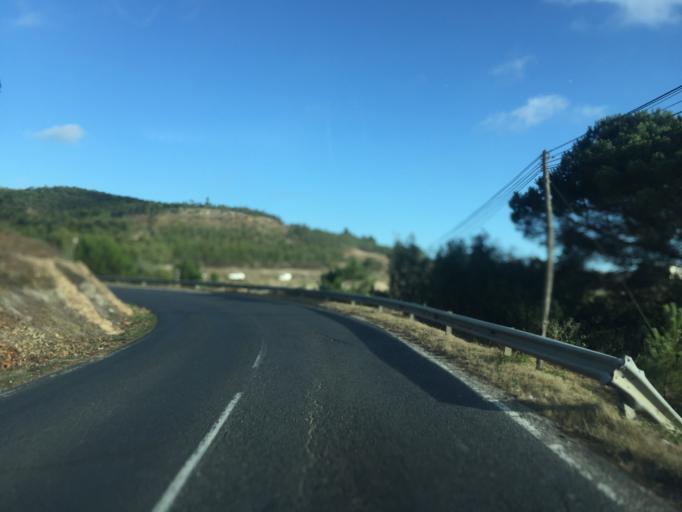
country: PT
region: Lisbon
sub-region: Torres Vedras
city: Torres Vedras
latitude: 39.1292
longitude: -9.2631
